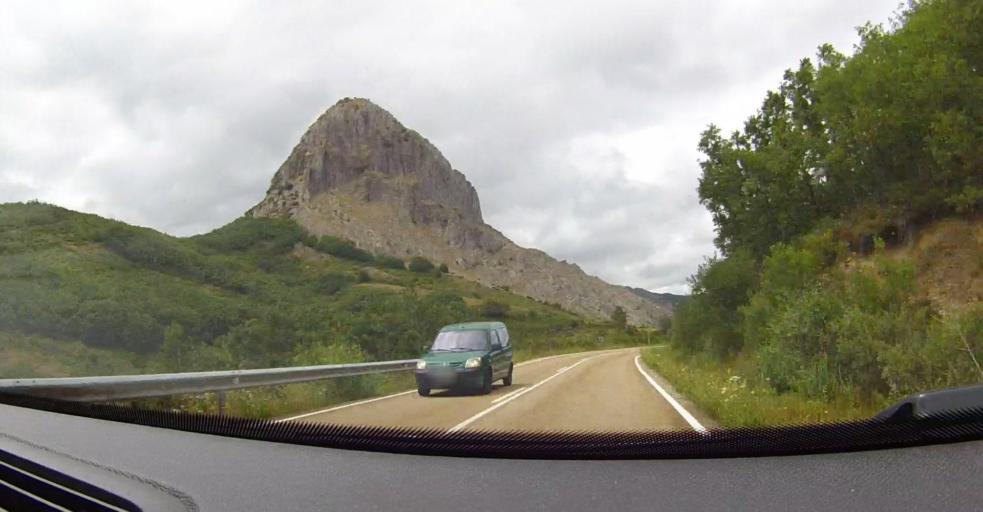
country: ES
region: Castille and Leon
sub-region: Provincia de Leon
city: Reyero
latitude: 42.9540
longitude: -5.2486
